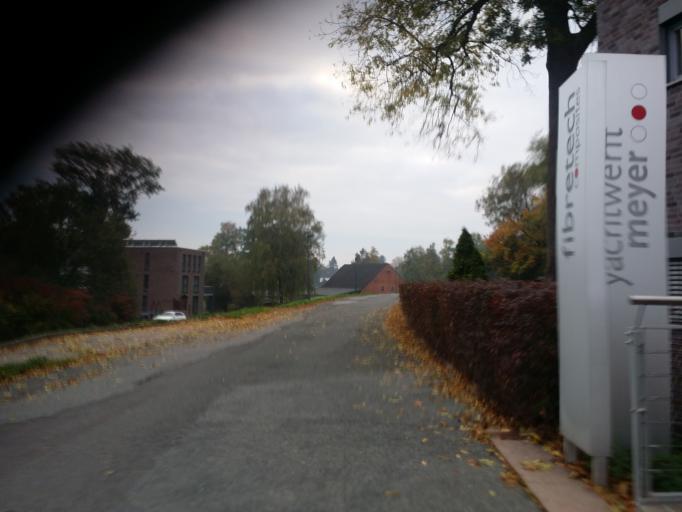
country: DE
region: Lower Saxony
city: Ritterhude
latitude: 53.1592
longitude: 8.7097
